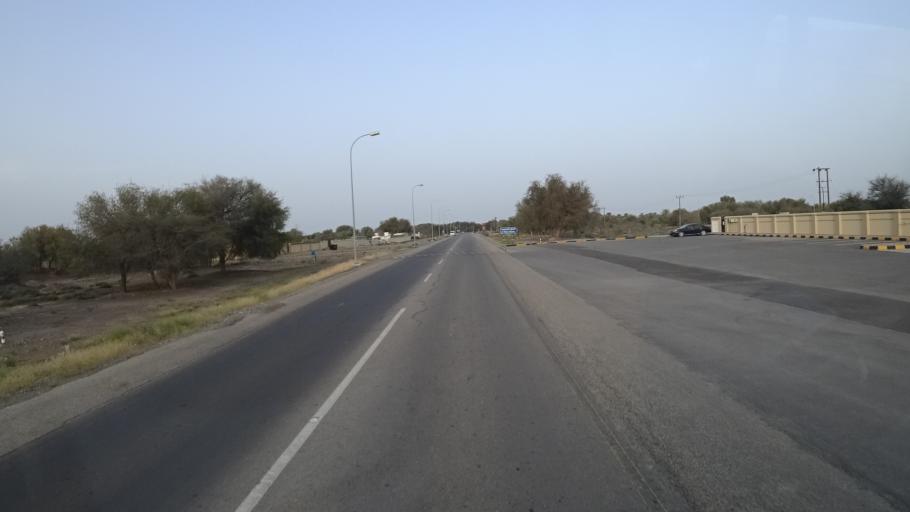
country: OM
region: Muhafazat Masqat
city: Muscat
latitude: 23.2055
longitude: 58.9576
